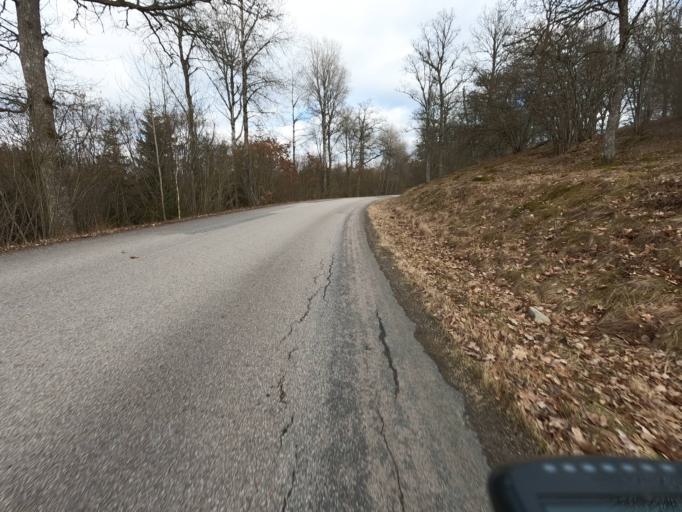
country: SE
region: Kronoberg
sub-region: Alvesta Kommun
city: Vislanda
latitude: 56.8215
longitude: 14.5161
